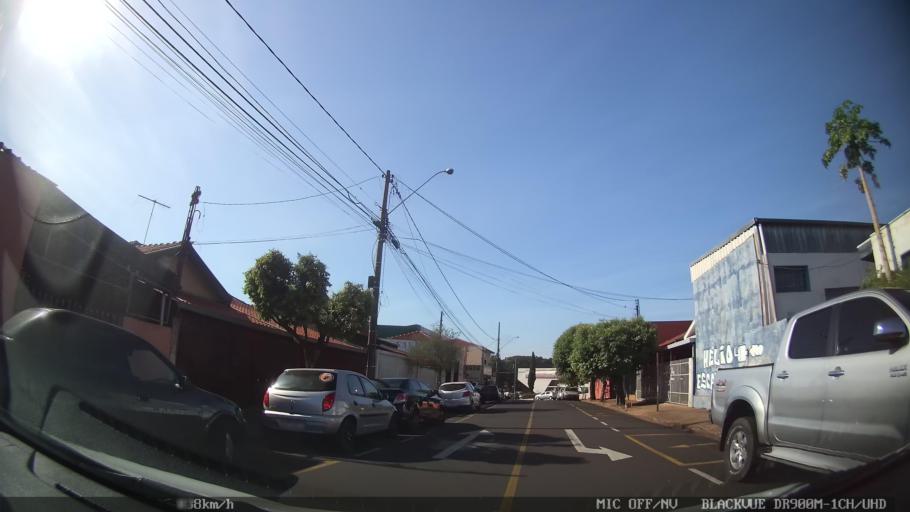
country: BR
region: Sao Paulo
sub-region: Sao Jose Do Rio Preto
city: Sao Jose do Rio Preto
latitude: -20.8246
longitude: -49.3746
